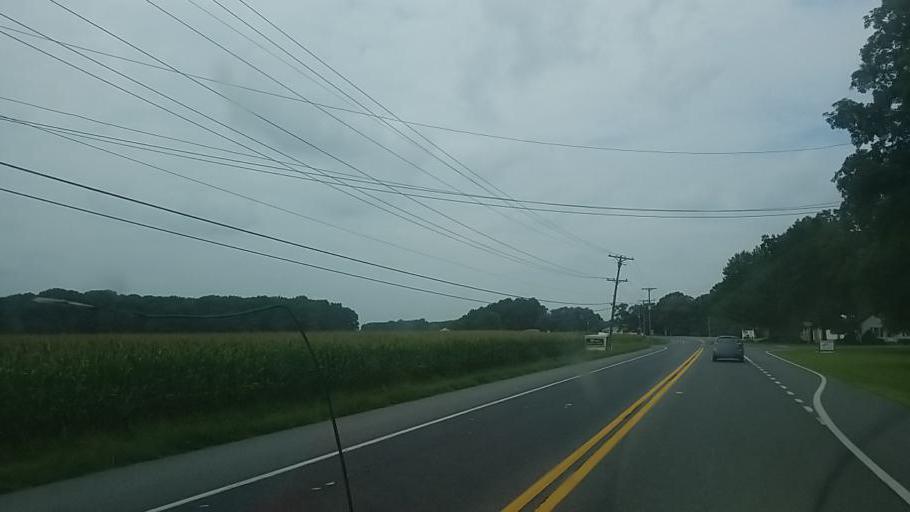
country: US
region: Delaware
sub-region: Sussex County
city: Long Neck
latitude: 38.5567
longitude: -75.1627
